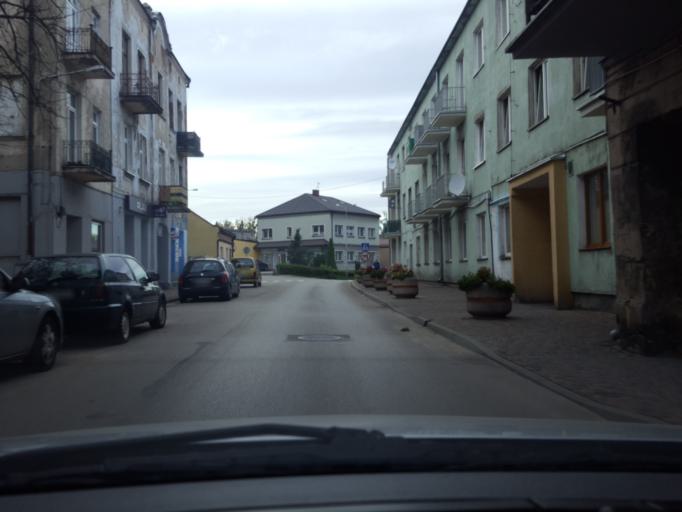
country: PL
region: Lodz Voivodeship
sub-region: Powiat brzezinski
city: Brzeziny
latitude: 51.8000
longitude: 19.7547
